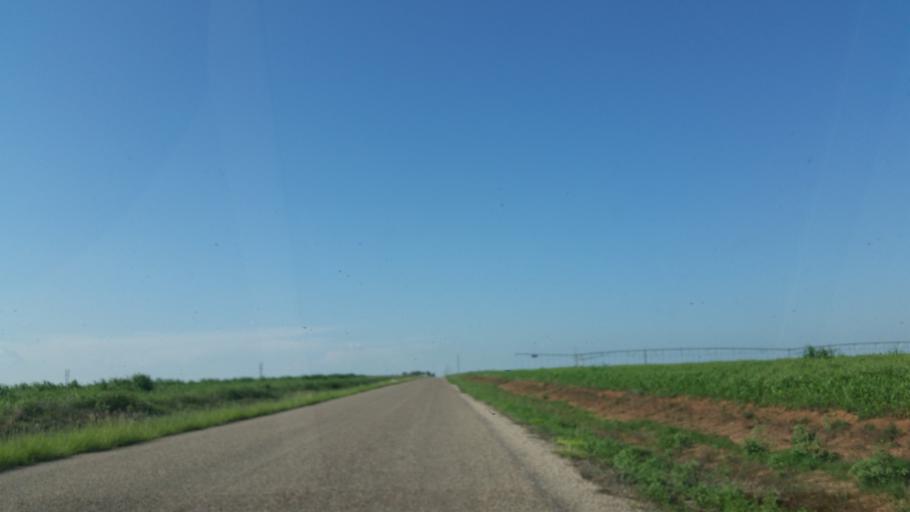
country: US
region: New Mexico
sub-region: Curry County
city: Clovis
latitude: 34.4499
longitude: -103.2317
